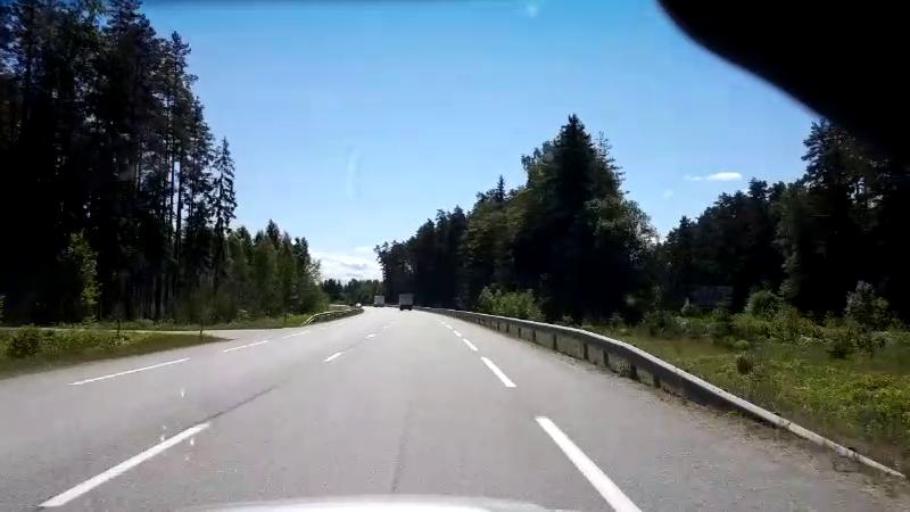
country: LV
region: Saulkrastu
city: Saulkrasti
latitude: 57.3444
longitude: 24.4425
